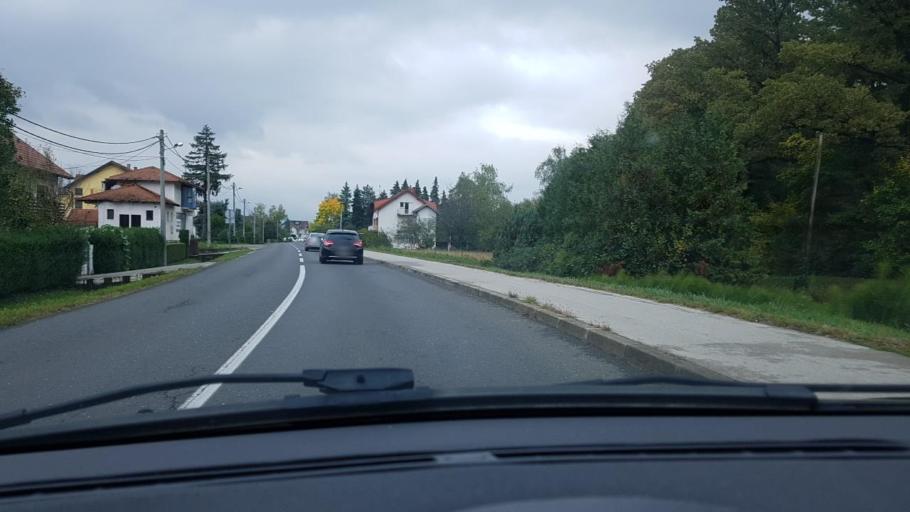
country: HR
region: Grad Zagreb
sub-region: Sesvete
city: Sesvete
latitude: 45.8460
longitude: 16.1100
